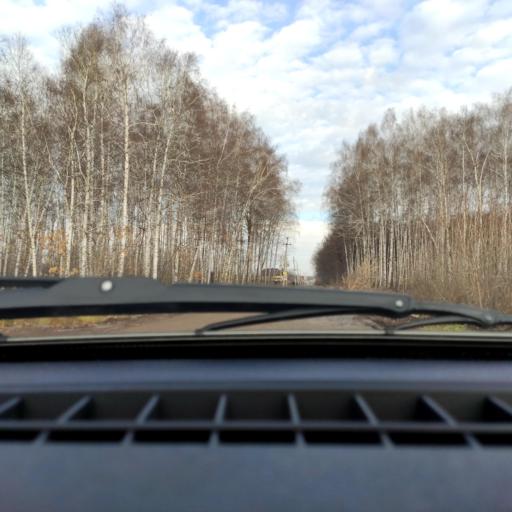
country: RU
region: Bashkortostan
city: Ufa
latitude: 54.6275
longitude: 55.8904
